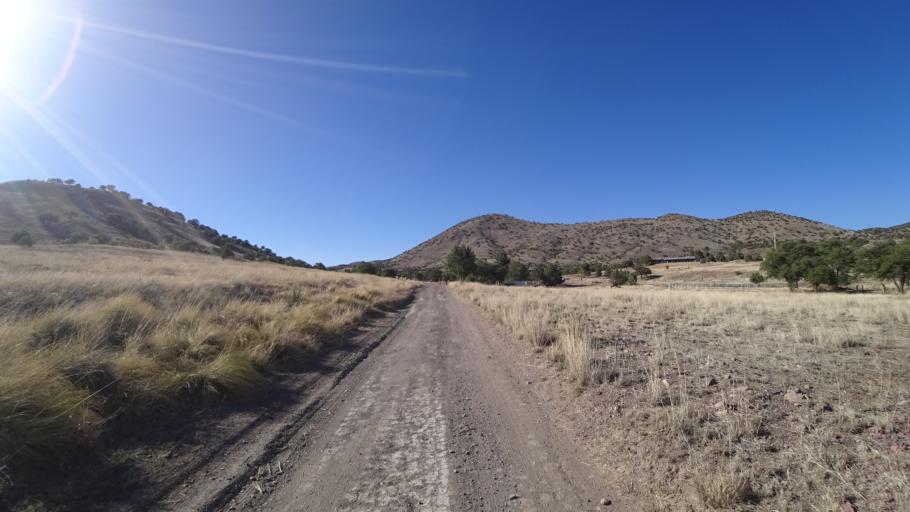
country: MX
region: Sonora
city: Santa Cruz
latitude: 31.4919
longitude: -110.5723
